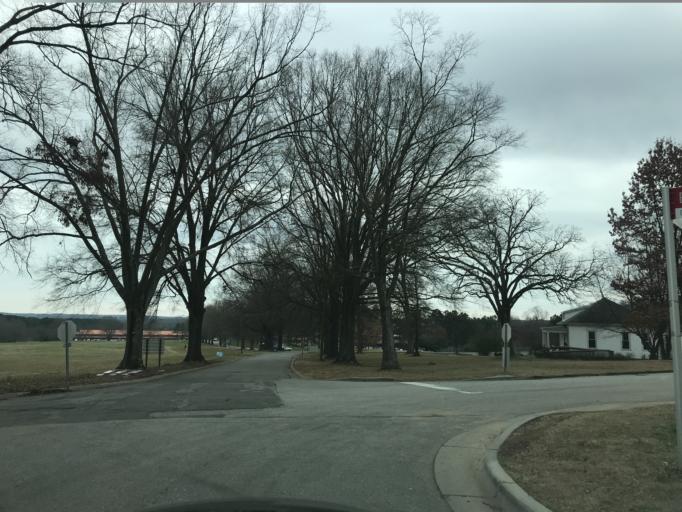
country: US
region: North Carolina
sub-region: Wake County
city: West Raleigh
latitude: 35.7705
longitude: -78.6653
